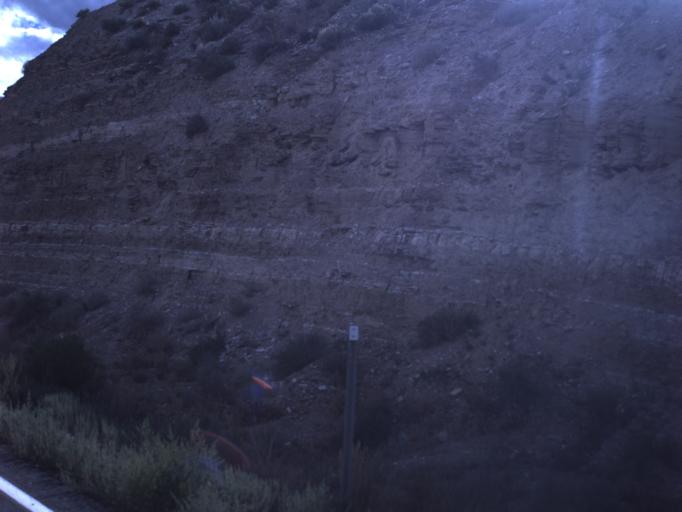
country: US
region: Utah
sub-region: Duchesne County
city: Duchesne
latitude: 40.1195
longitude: -110.4494
